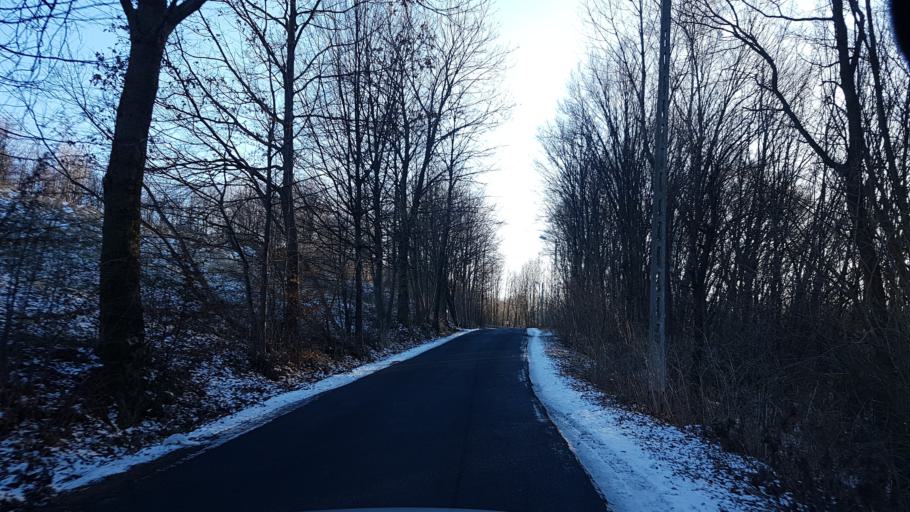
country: PL
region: Lesser Poland Voivodeship
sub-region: Powiat nowosadecki
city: Rytro
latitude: 49.5163
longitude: 20.6616
